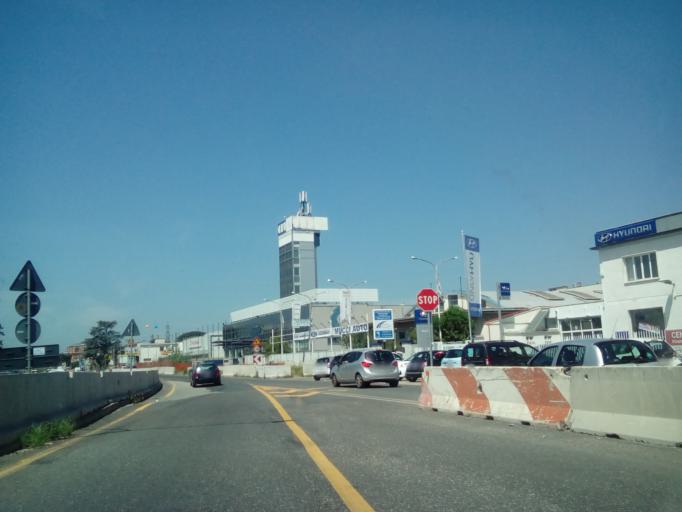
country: IT
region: Latium
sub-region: Citta metropolitana di Roma Capitale
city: Colle Verde
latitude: 41.9331
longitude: 12.5919
